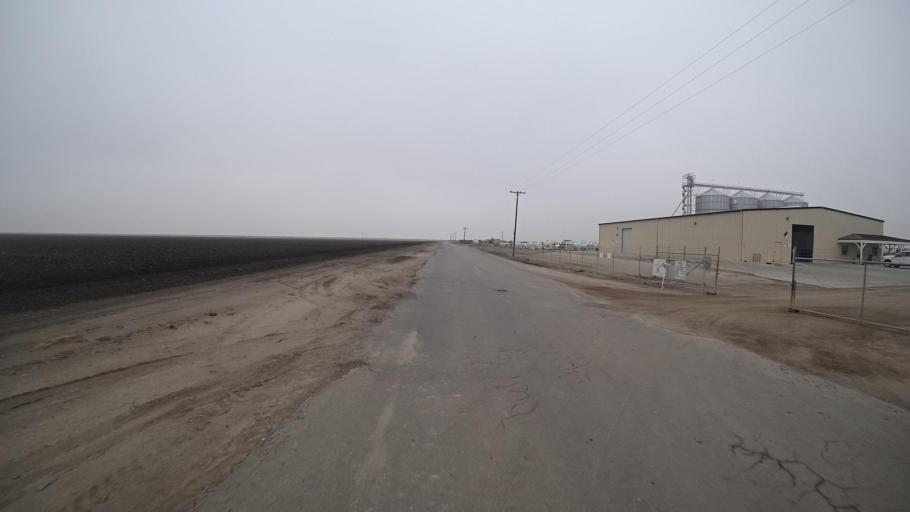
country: US
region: California
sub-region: Kern County
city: Rosedale
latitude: 35.1944
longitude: -119.2276
